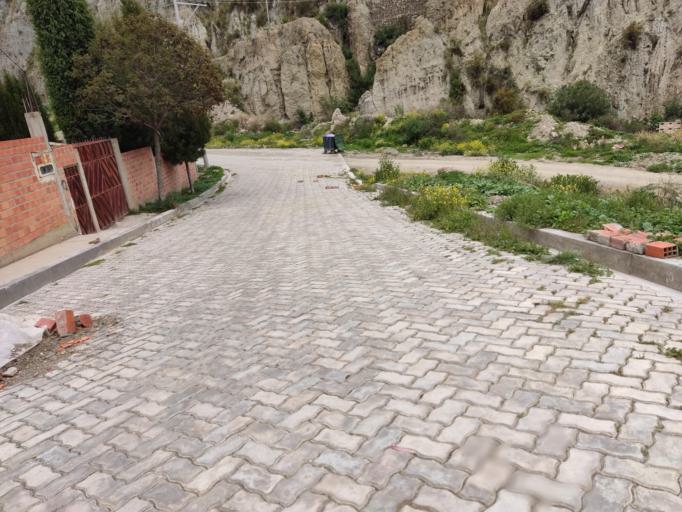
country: BO
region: La Paz
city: La Paz
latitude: -16.5354
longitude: -68.1302
